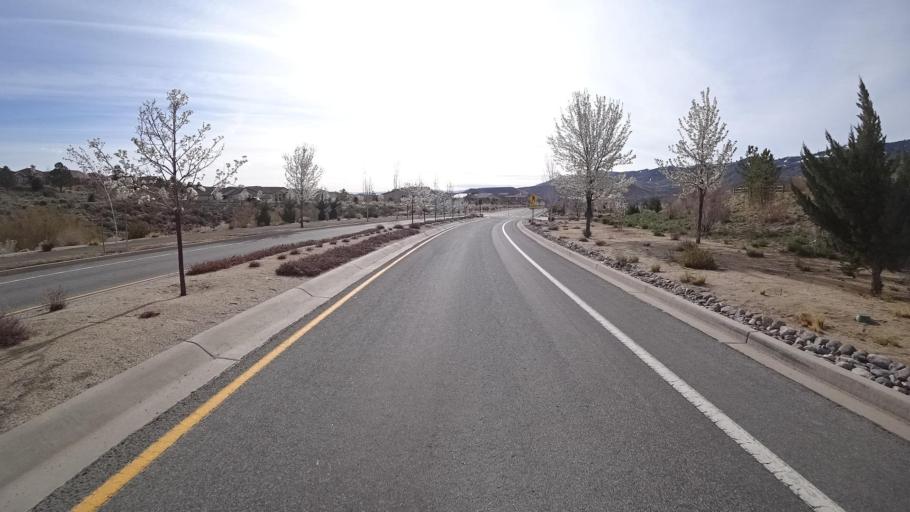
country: US
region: Nevada
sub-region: Washoe County
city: Mogul
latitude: 39.5188
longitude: -119.9450
